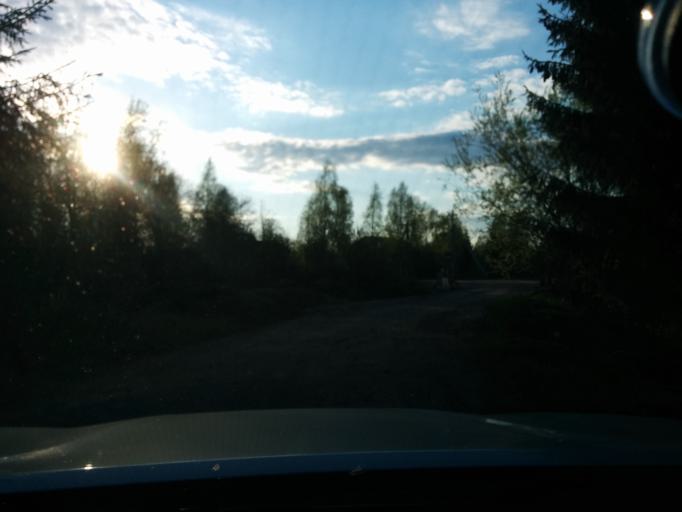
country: RU
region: Leningrad
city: Verkhniye Osel'ki
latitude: 60.2598
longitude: 30.4147
